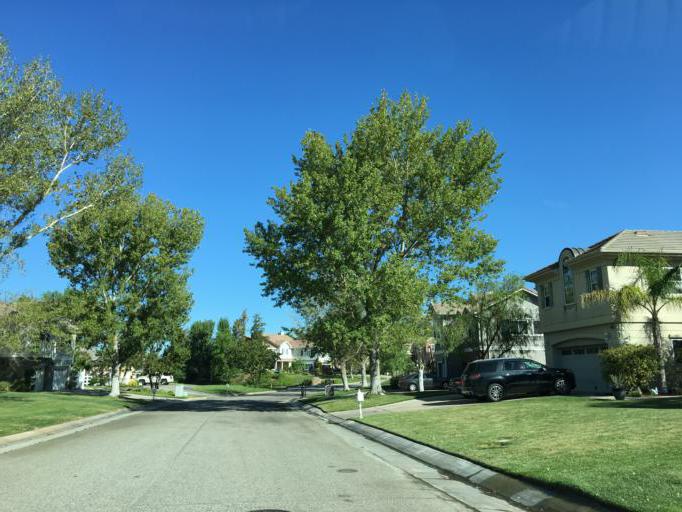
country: US
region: California
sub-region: Los Angeles County
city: Agua Dulce
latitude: 34.4007
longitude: -118.4019
